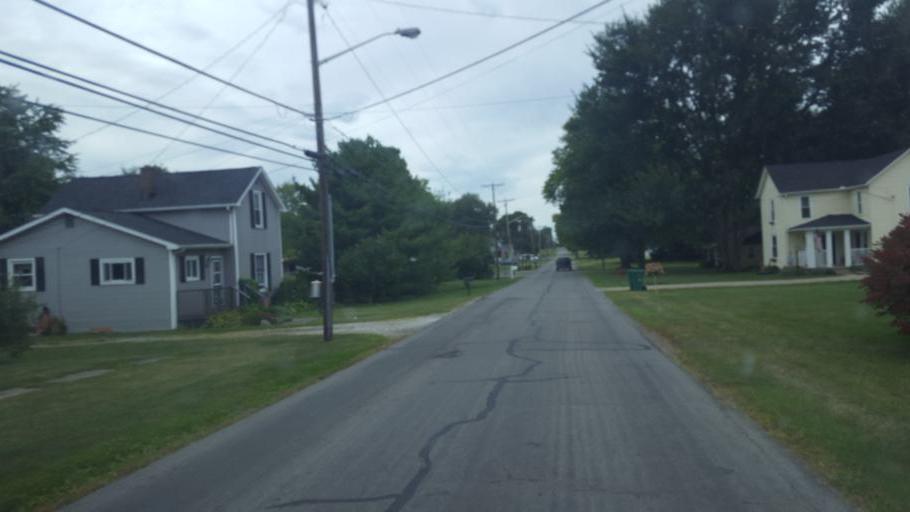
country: US
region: Ohio
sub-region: Knox County
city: Centerburg
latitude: 40.3067
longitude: -82.7018
